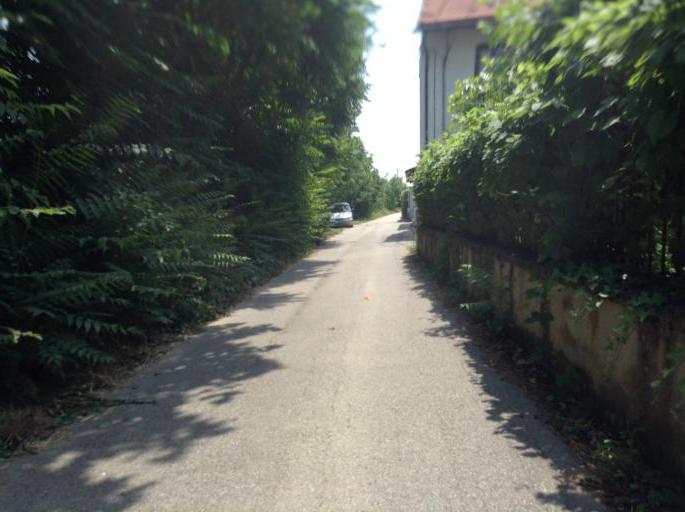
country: IT
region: Piedmont
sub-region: Provincia di Torino
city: Carignano
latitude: 44.9005
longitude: 7.6747
